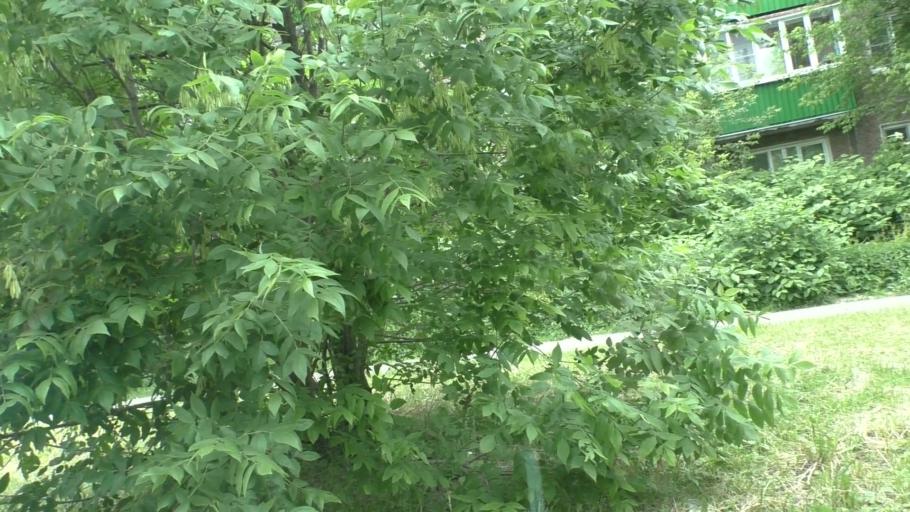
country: RU
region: Moskovskaya
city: Yegor'yevsk
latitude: 55.3672
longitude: 39.0649
